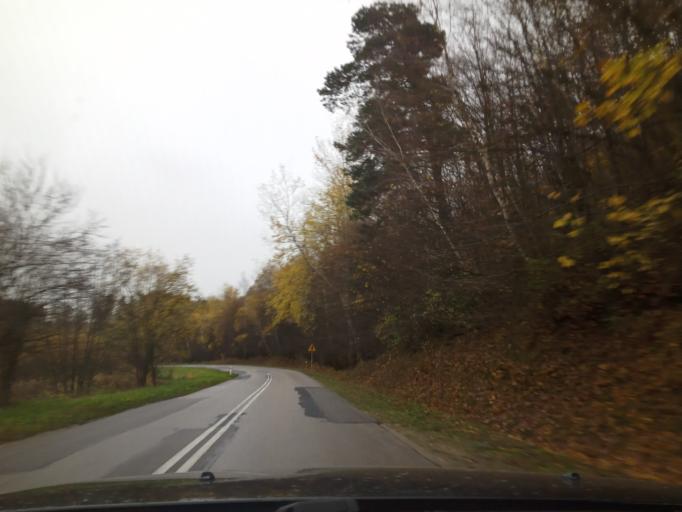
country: PL
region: Swietokrzyskie
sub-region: Powiat pinczowski
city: Dzialoszyce
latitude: 50.4163
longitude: 20.3322
